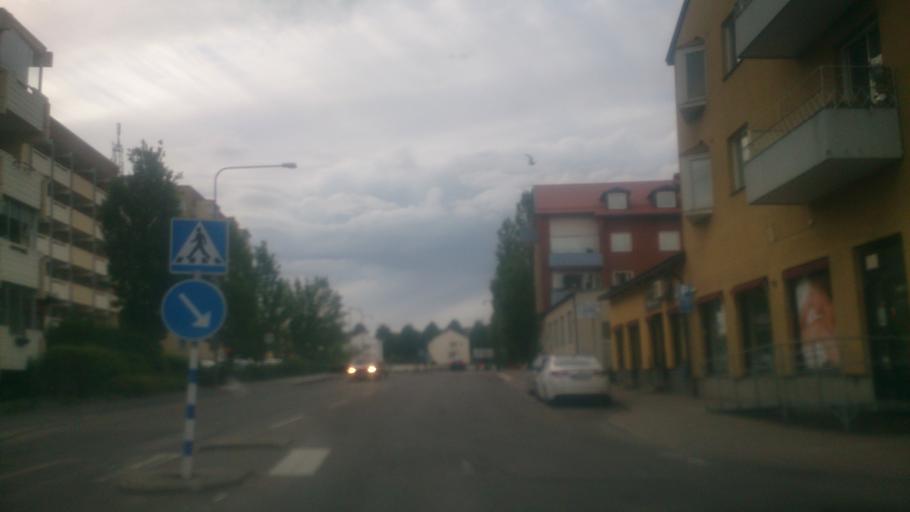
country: SE
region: OEstergoetland
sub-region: Motala Kommun
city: Motala
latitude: 58.5365
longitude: 15.0328
